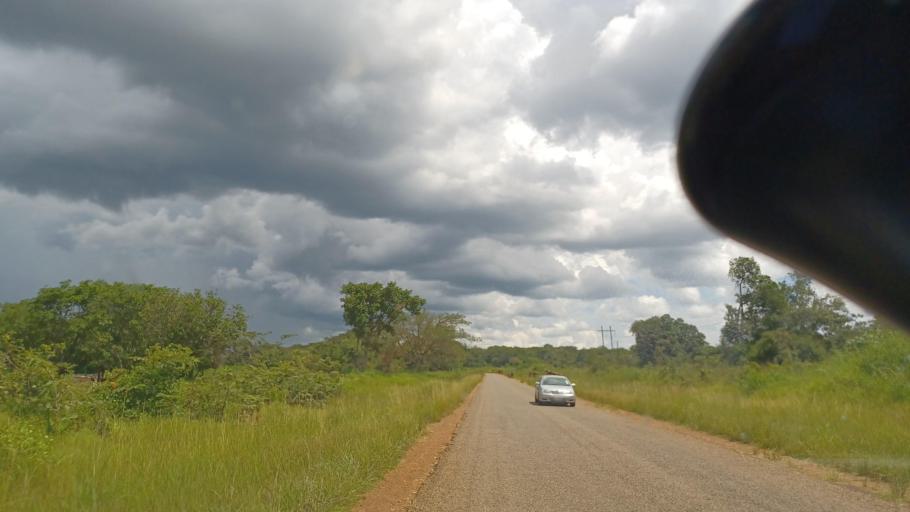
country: ZM
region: North-Western
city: Kasempa
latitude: -12.7766
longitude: 26.0109
